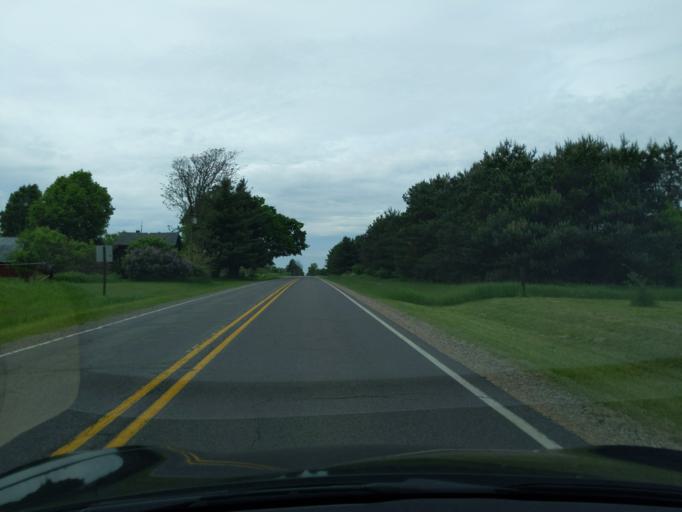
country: US
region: Michigan
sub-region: Ingham County
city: Leslie
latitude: 42.4721
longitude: -84.3561
